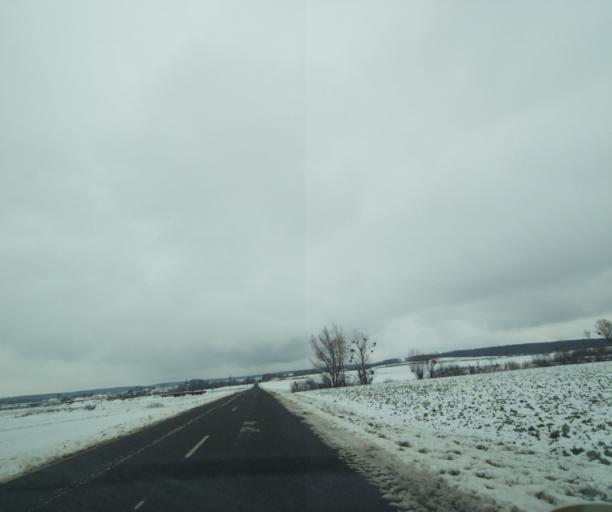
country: FR
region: Champagne-Ardenne
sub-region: Departement de la Haute-Marne
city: Laneuville-a-Remy
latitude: 48.4170
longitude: 4.8256
